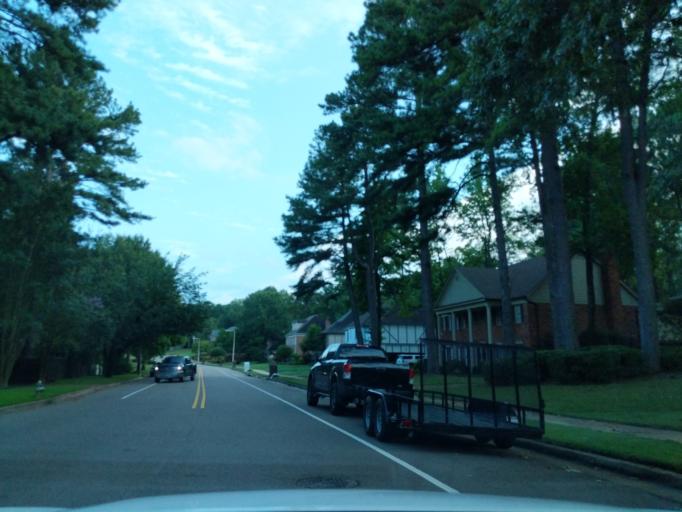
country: US
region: Tennessee
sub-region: Shelby County
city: Germantown
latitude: 35.0692
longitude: -89.7783
